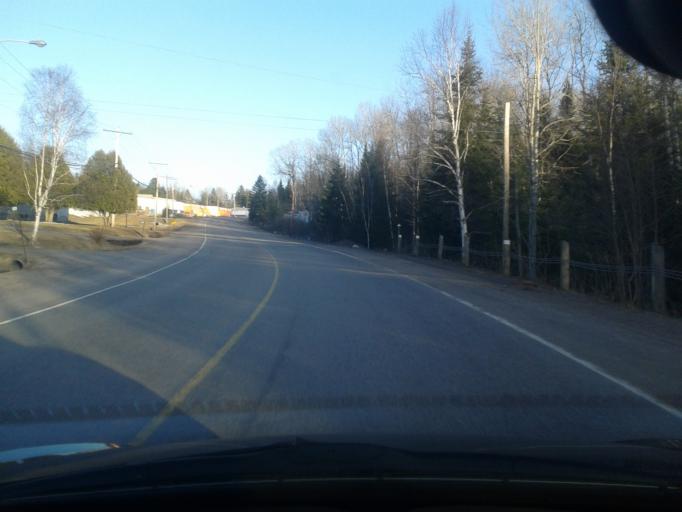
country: CA
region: Ontario
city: Powassan
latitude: 46.1878
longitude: -79.2905
